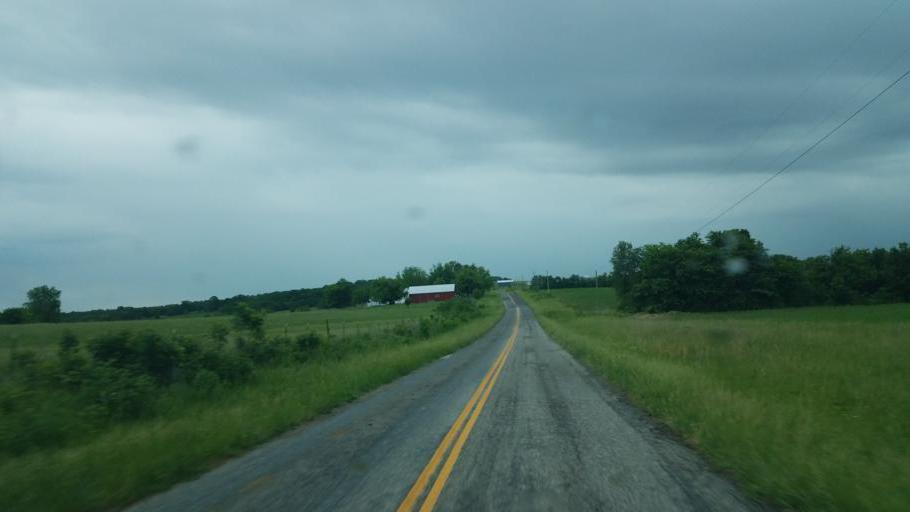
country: US
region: Missouri
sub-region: Moniteau County
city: California
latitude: 38.7715
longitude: -92.6052
